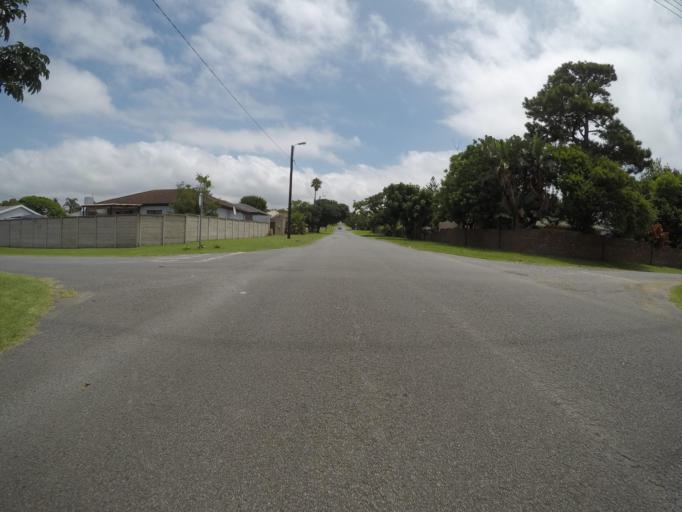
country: ZA
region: Eastern Cape
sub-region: Buffalo City Metropolitan Municipality
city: East London
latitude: -32.9436
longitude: 28.0084
